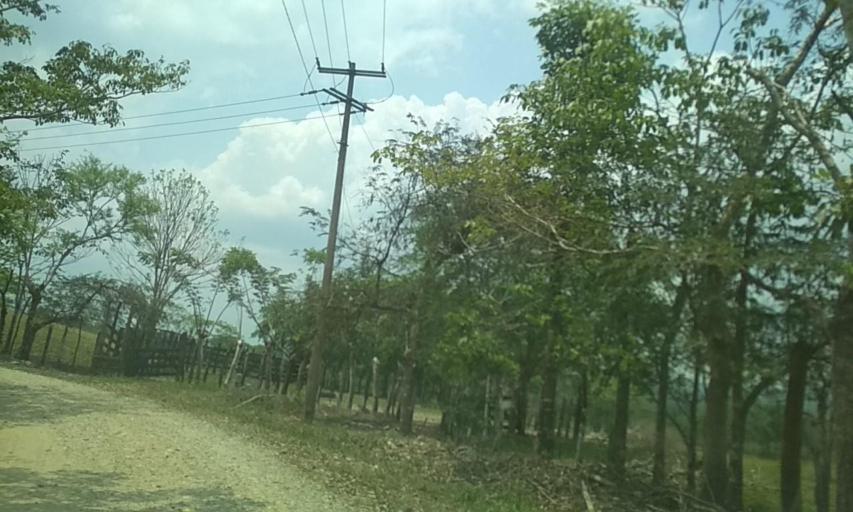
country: MX
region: Tabasco
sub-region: Huimanguillo
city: Francisco Rueda
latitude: 17.5843
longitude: -93.7906
